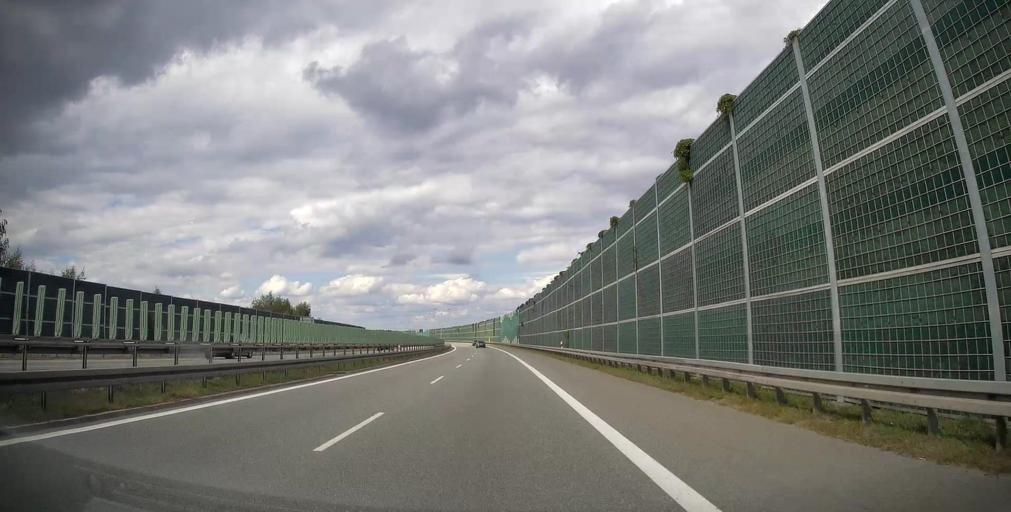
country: PL
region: Masovian Voivodeship
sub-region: Powiat bialobrzeski
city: Stara Blotnica
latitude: 51.5639
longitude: 21.0272
